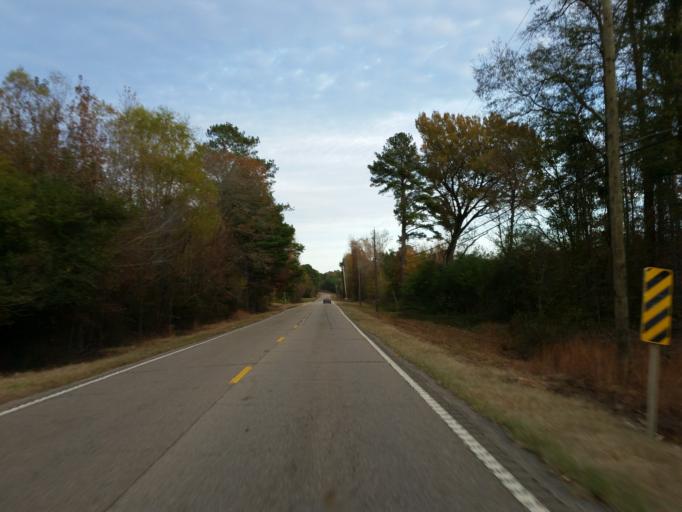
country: US
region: Mississippi
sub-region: Lauderdale County
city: Marion
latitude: 32.4121
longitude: -88.5526
